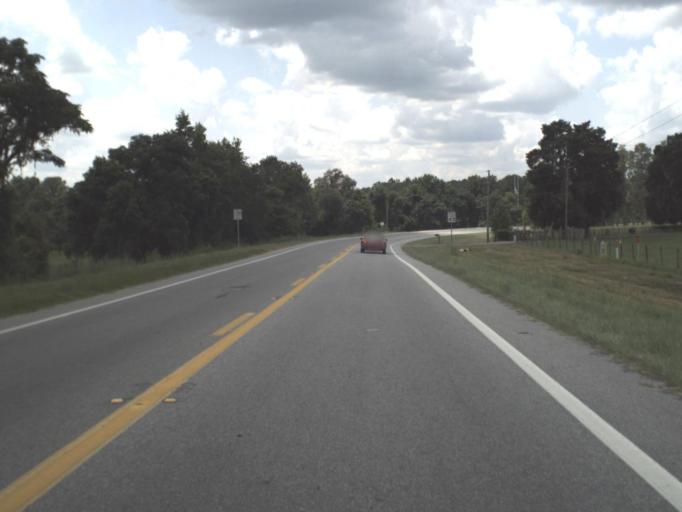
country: US
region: Florida
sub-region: Hamilton County
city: Jasper
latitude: 30.5047
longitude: -82.9434
